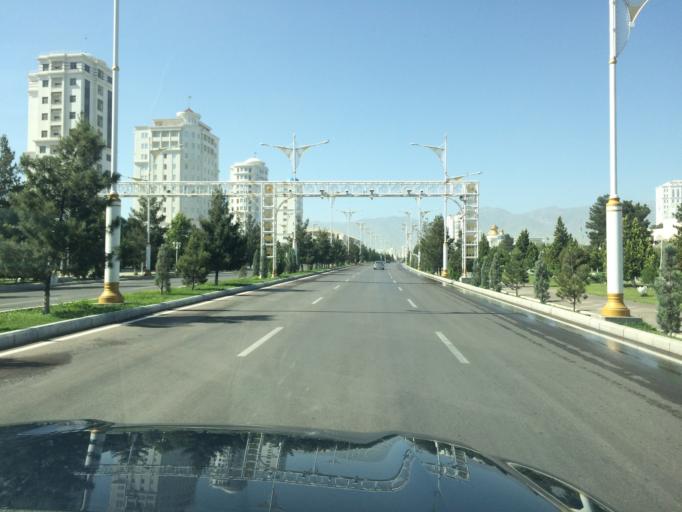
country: TM
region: Ahal
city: Ashgabat
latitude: 37.9220
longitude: 58.3750
